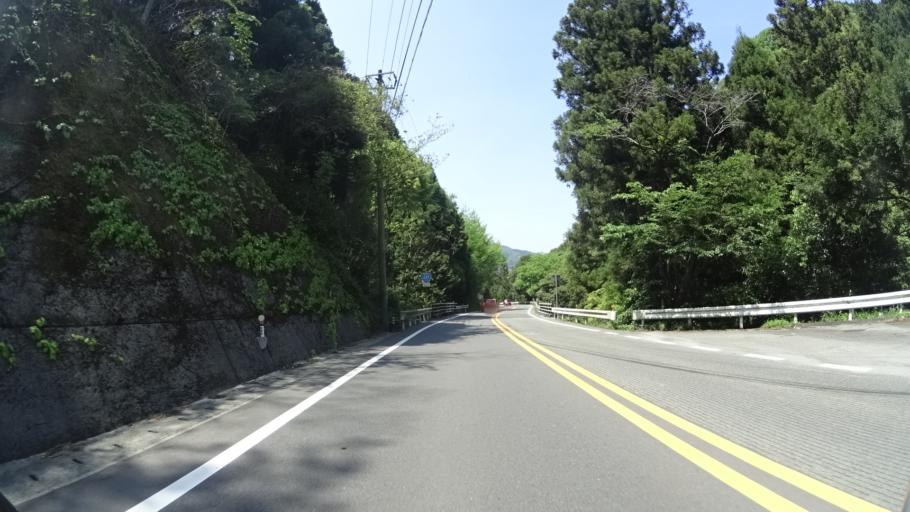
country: JP
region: Ehime
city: Hojo
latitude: 33.9619
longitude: 132.9077
